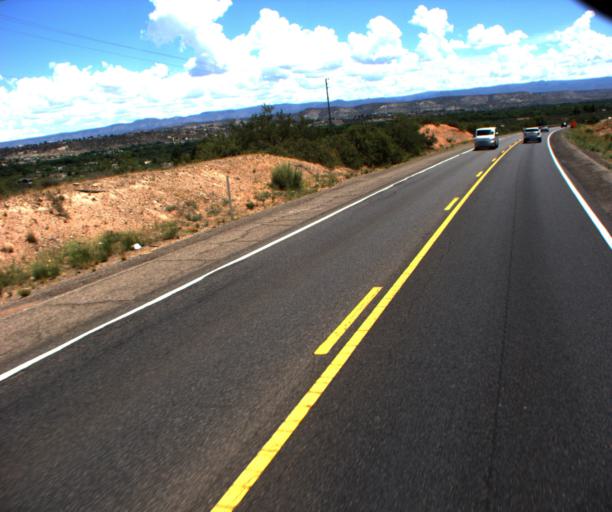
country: US
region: Arizona
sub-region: Yavapai County
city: Camp Verde
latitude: 34.5982
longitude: -111.8970
